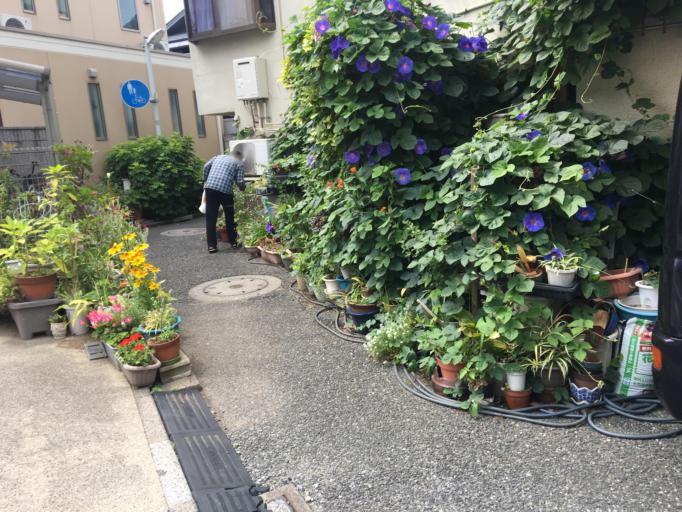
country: JP
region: Chiba
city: Matsudo
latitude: 35.7337
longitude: 139.8509
